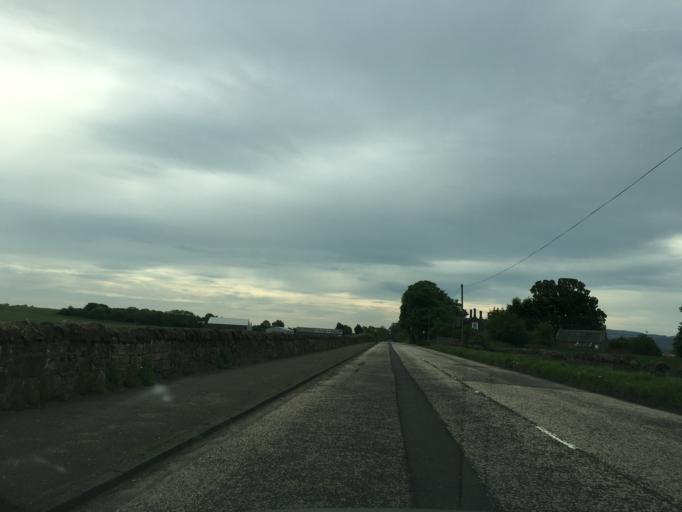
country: GB
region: Scotland
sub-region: Edinburgh
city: Currie
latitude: 55.9462
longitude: -3.3264
